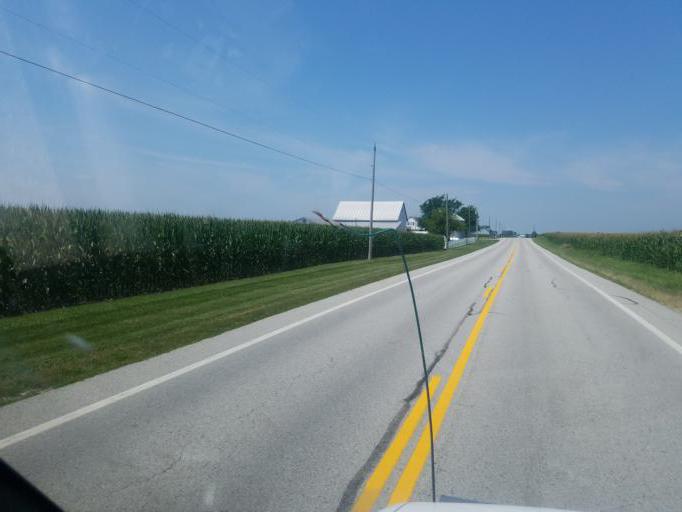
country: US
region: Ohio
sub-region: Auglaize County
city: New Bremen
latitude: 40.4415
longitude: -84.4339
